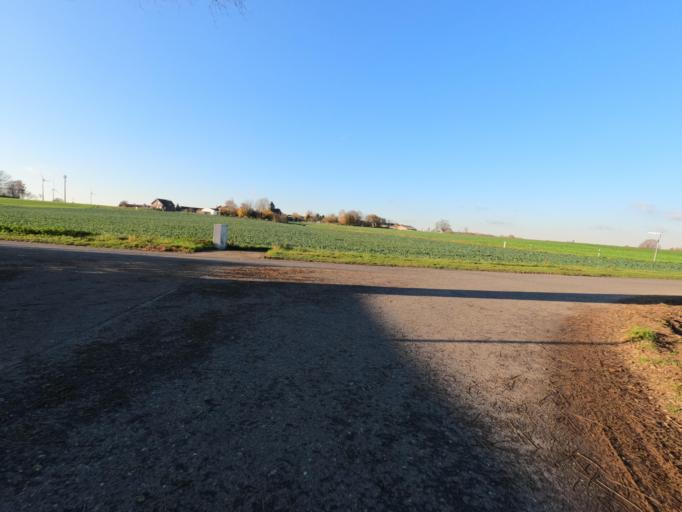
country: DE
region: North Rhine-Westphalia
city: Geilenkirchen
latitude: 51.0193
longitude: 6.1394
